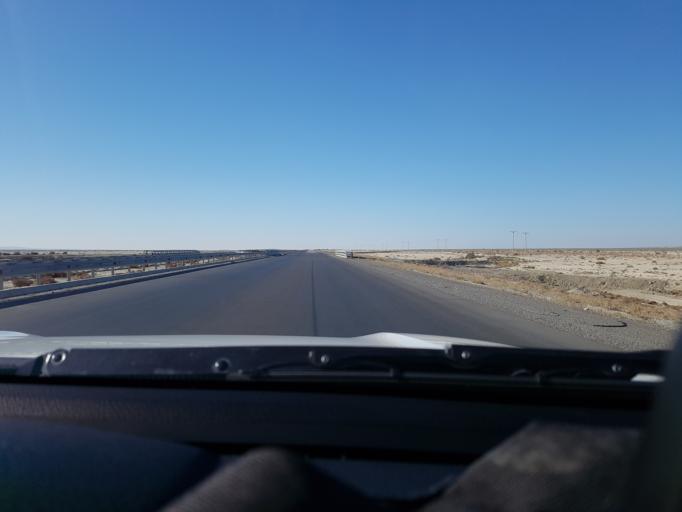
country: TM
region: Balkan
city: Gazanjyk
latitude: 39.2582
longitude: 55.1097
